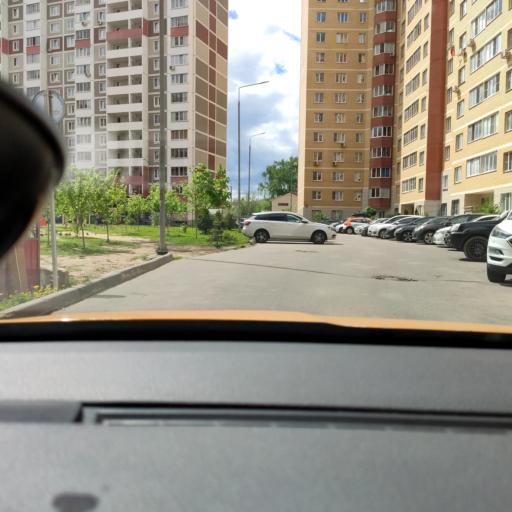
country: RU
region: Moskovskaya
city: Novopodrezkovo
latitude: 55.9485
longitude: 37.3320
